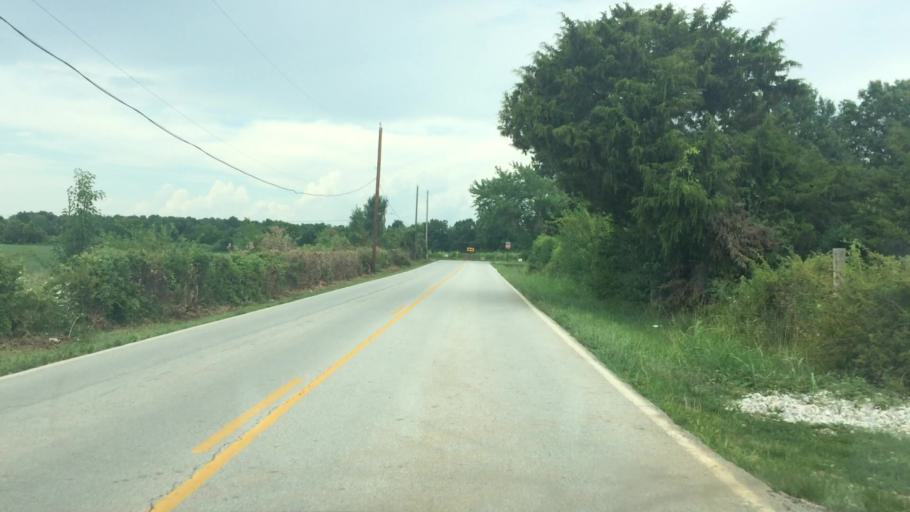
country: US
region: Missouri
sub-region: Greene County
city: Strafford
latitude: 37.2546
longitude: -93.1832
